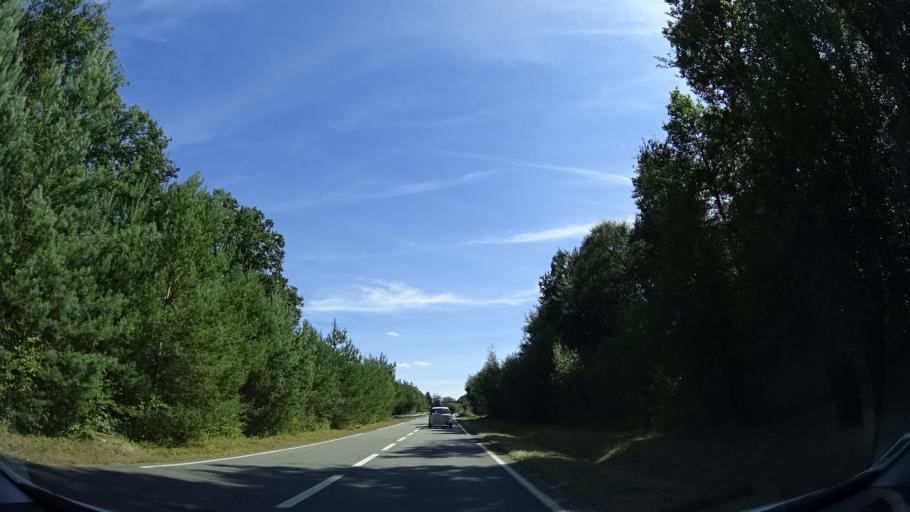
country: FR
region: Brittany
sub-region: Departement d'Ille-et-Vilaine
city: Liffre
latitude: 48.2027
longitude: -1.5302
